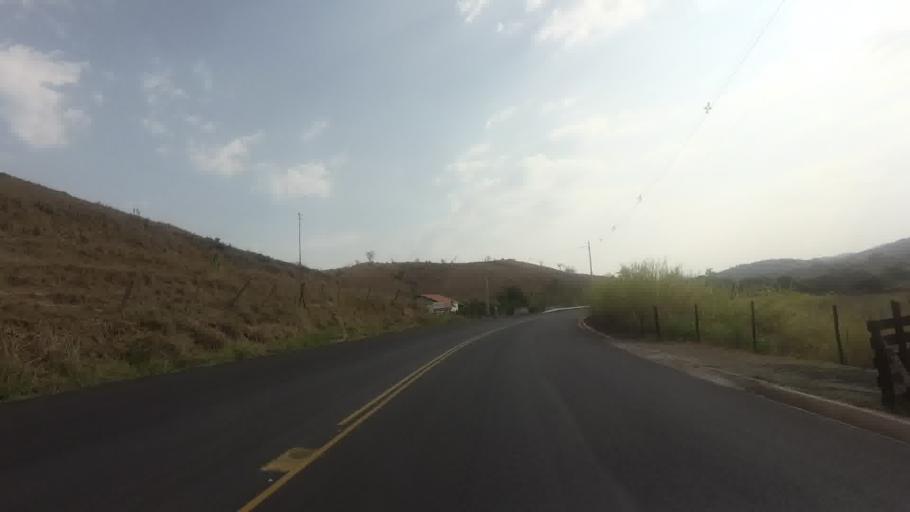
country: BR
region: Rio de Janeiro
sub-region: Itaperuna
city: Itaperuna
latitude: -21.3073
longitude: -41.8507
